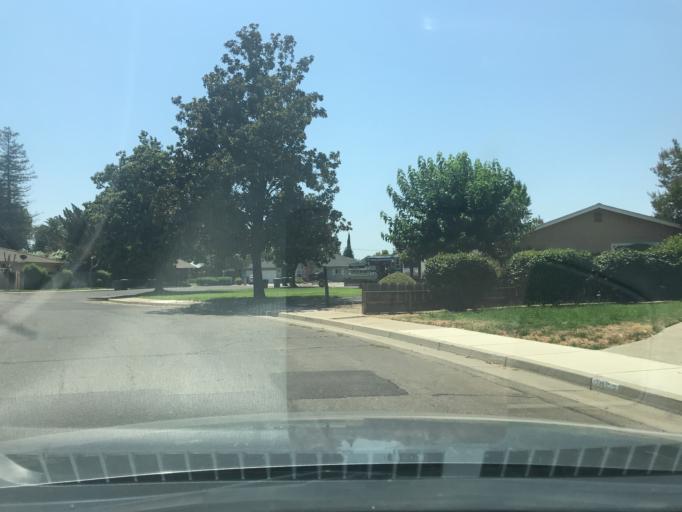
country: US
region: California
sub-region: Merced County
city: Atwater
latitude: 37.3657
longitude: -120.6082
